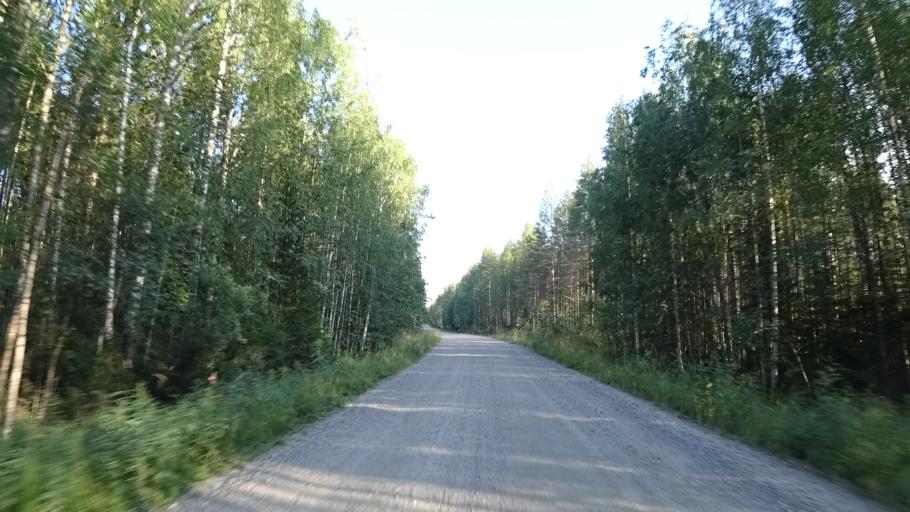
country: FI
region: North Karelia
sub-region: Joensuu
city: Ilomantsi
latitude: 63.1340
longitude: 30.7078
